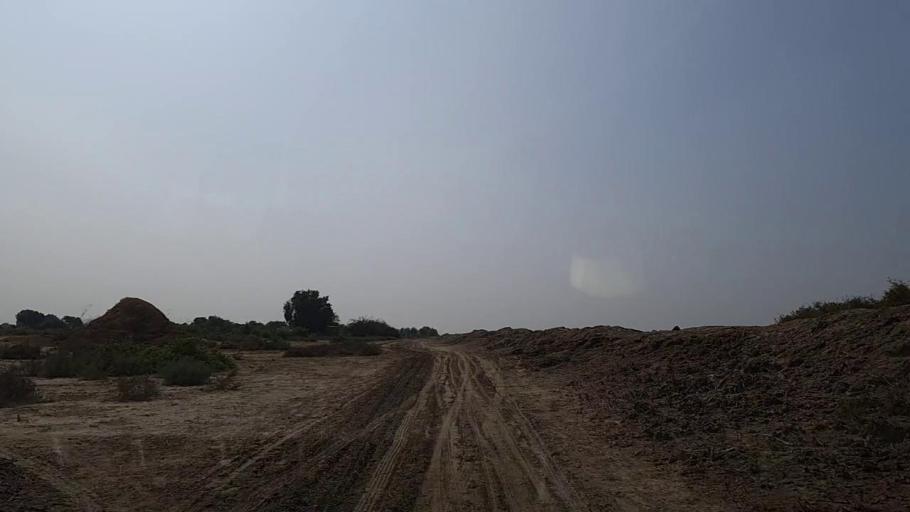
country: PK
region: Sindh
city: Mirpur Sakro
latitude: 24.5455
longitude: 67.7898
